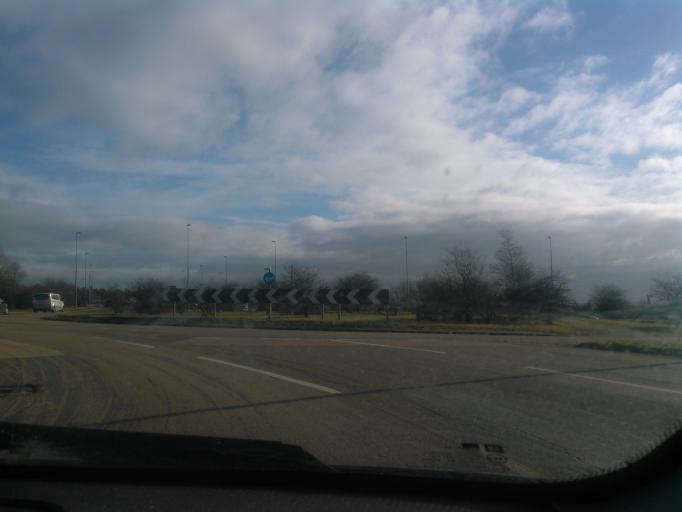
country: GB
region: England
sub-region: Staffordshire
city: Uttoxeter
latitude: 52.9078
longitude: -1.8537
